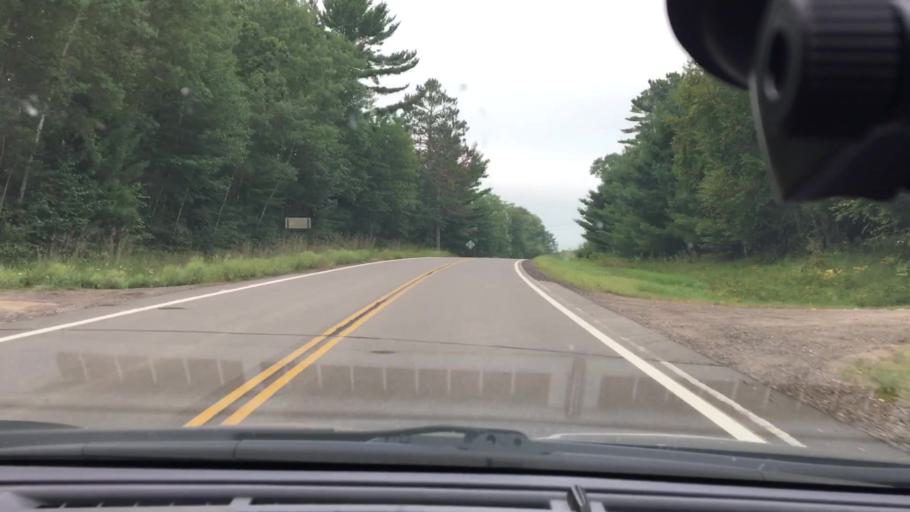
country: US
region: Minnesota
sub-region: Crow Wing County
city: Cross Lake
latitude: 46.6622
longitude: -93.9556
